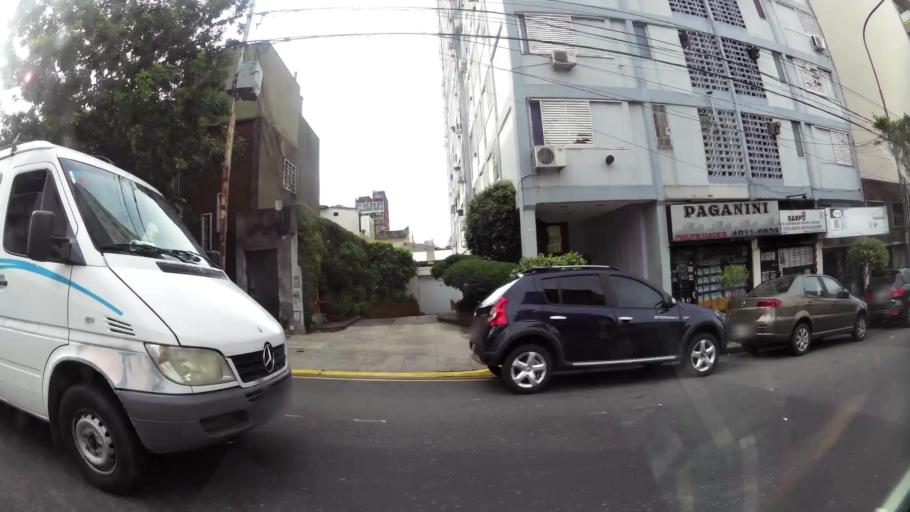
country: AR
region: Buenos Aires F.D.
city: Villa Santa Rita
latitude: -34.6361
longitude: -58.4696
